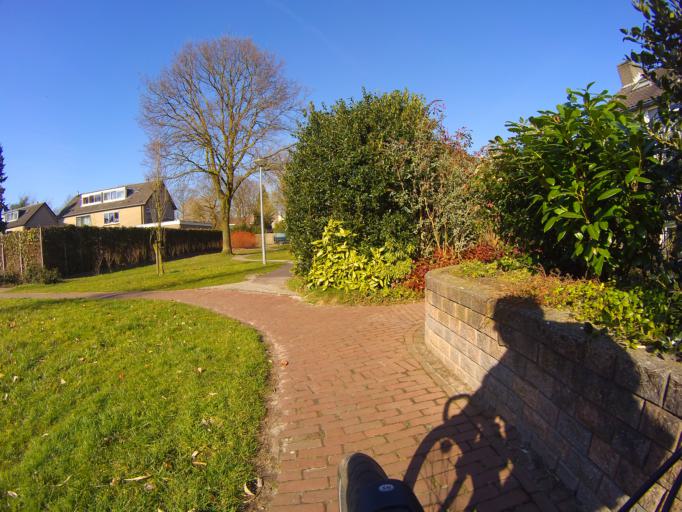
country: NL
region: Gelderland
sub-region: Gemeente Barneveld
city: Zwartebroek
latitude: 52.1707
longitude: 5.4599
